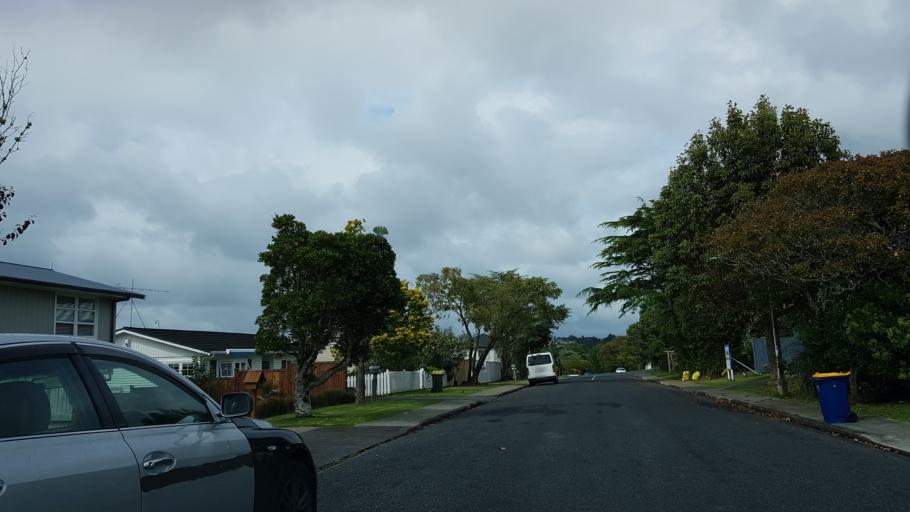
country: NZ
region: Auckland
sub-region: Auckland
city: North Shore
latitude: -36.7899
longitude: 174.7400
